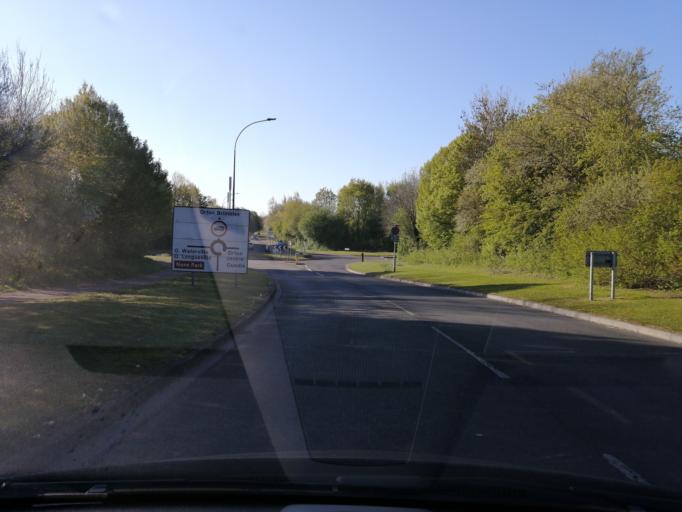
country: GB
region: England
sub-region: Peterborough
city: Castor
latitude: 52.5552
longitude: -0.3059
